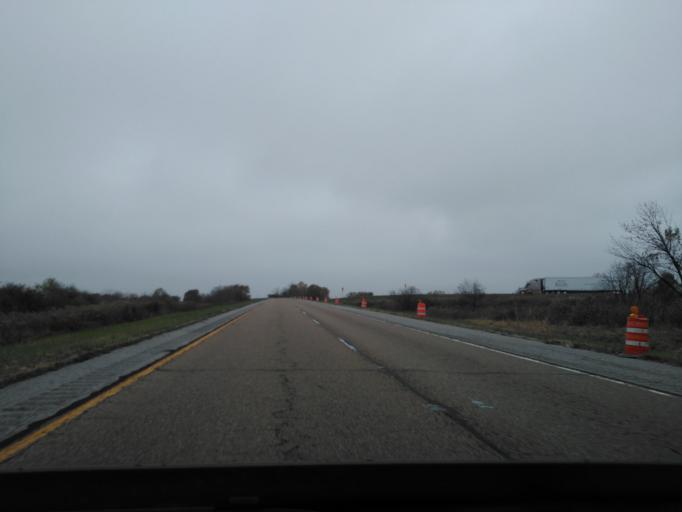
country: US
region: Illinois
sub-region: Madison County
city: Troy
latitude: 38.7510
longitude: -89.9035
